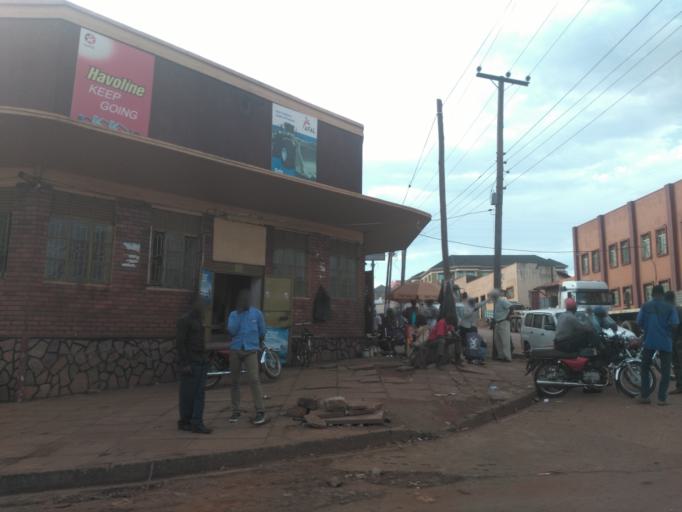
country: UG
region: Eastern Region
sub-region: Jinja District
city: Jinja
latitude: 0.4268
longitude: 33.2127
